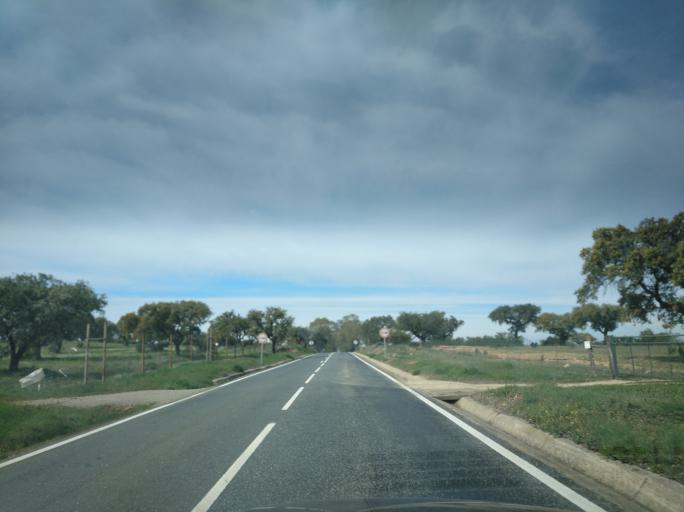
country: PT
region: Beja
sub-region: Mertola
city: Mertola
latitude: 37.7318
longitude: -7.7691
